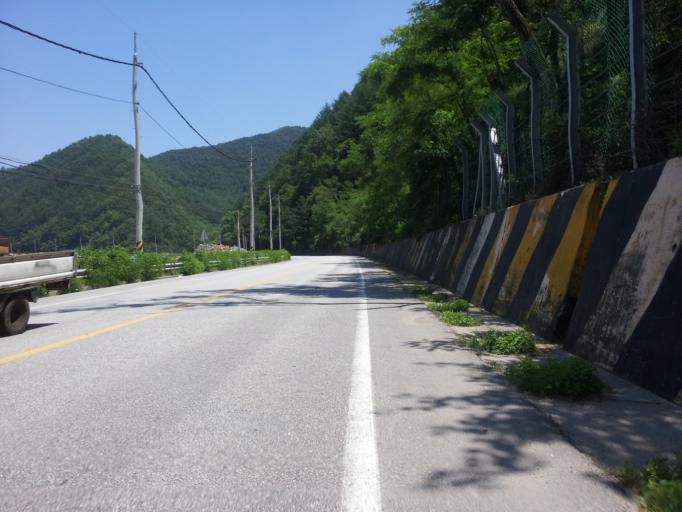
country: KR
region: Chungcheongbuk-do
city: Okcheon
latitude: 36.3684
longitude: 127.6389
